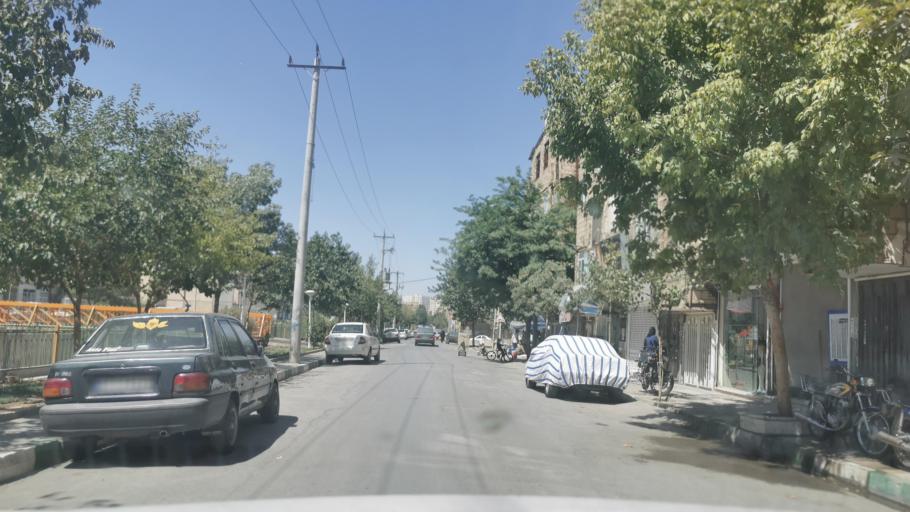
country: IR
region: Razavi Khorasan
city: Mashhad
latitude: 36.3593
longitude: 59.5615
